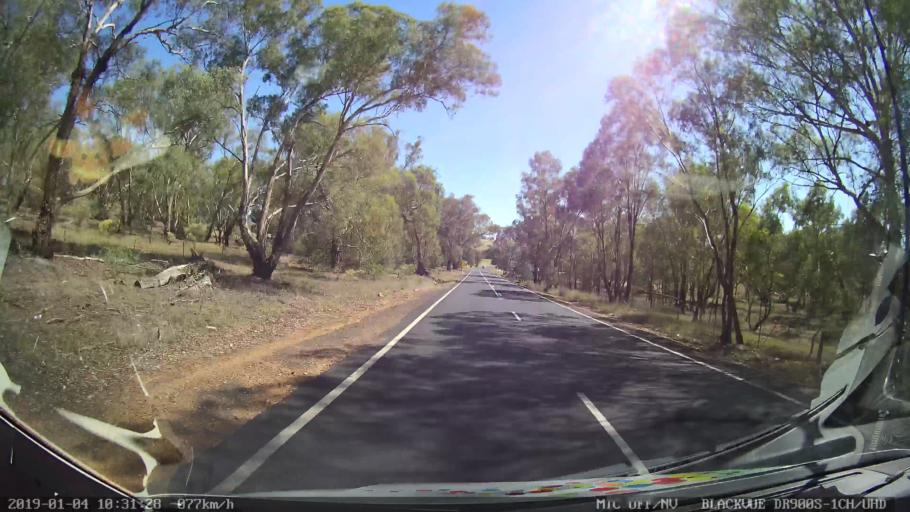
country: AU
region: New South Wales
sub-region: Cabonne
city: Canowindra
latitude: -33.3344
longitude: 148.6323
